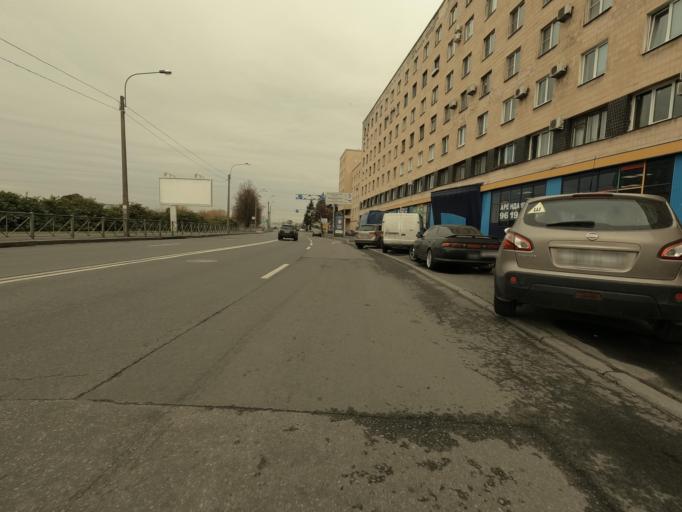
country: RU
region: St.-Petersburg
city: Centralniy
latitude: 59.9411
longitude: 30.4135
